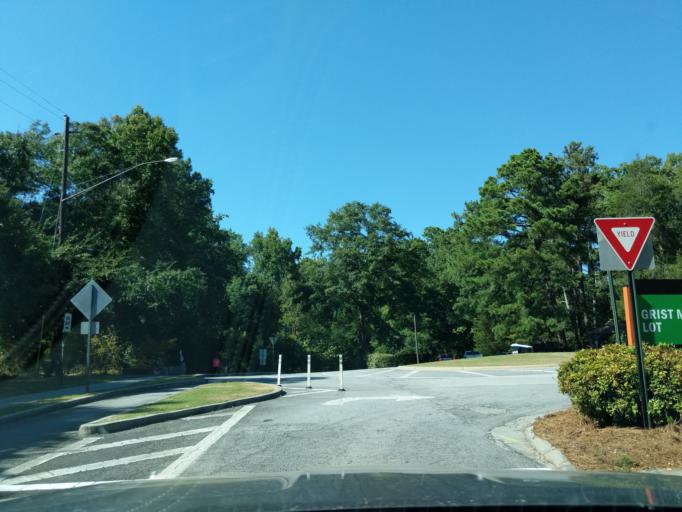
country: US
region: Georgia
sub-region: DeKalb County
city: Stone Mountain
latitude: 33.8048
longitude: -84.1352
